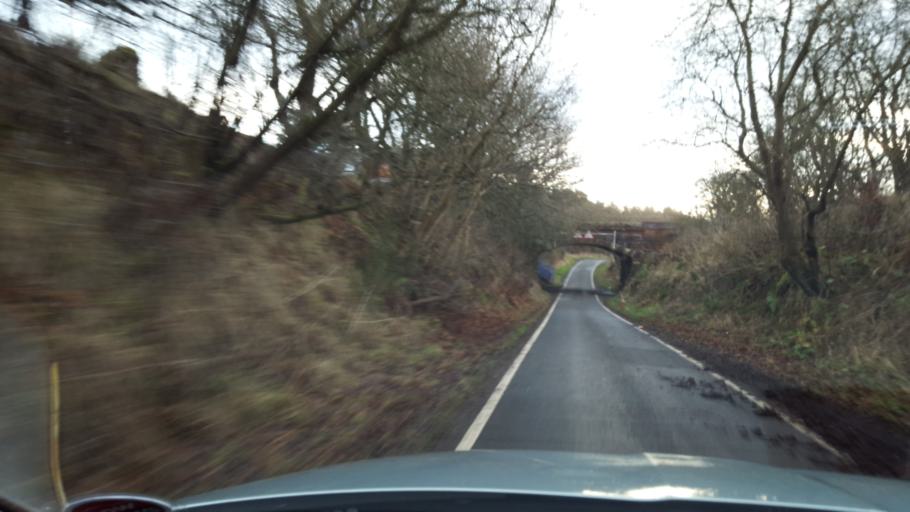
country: GB
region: Scotland
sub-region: West Lothian
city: Mid Calder
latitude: 55.8525
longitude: -3.5087
